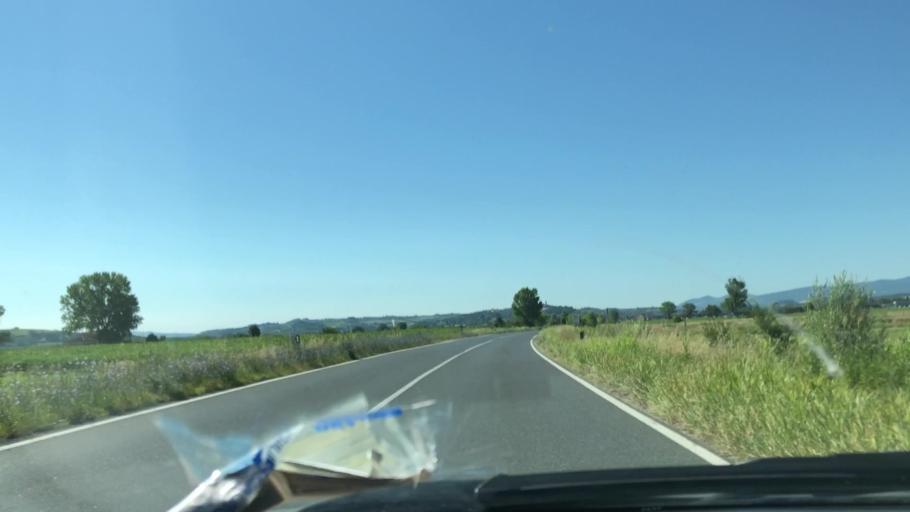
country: IT
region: Tuscany
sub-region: Province of Pisa
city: Forcoli
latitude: 43.5914
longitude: 10.7005
